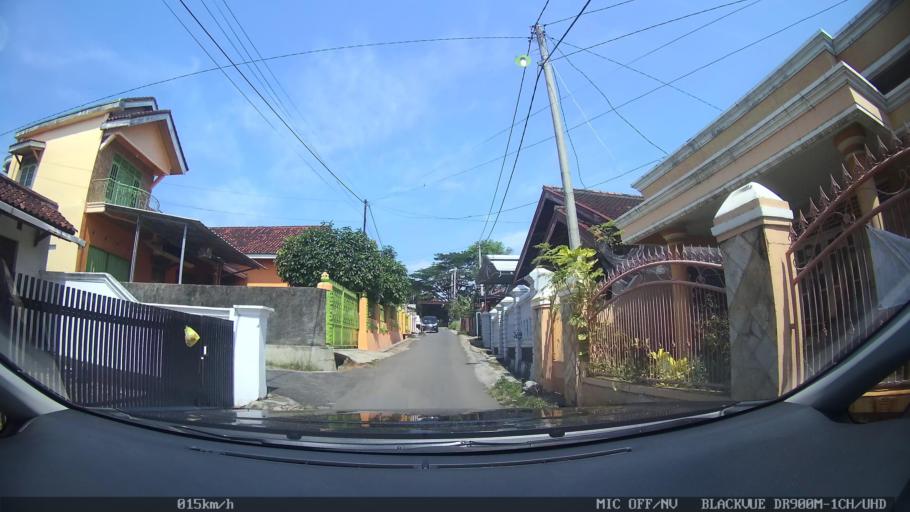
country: ID
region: Lampung
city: Kedaton
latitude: -5.3692
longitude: 105.2545
